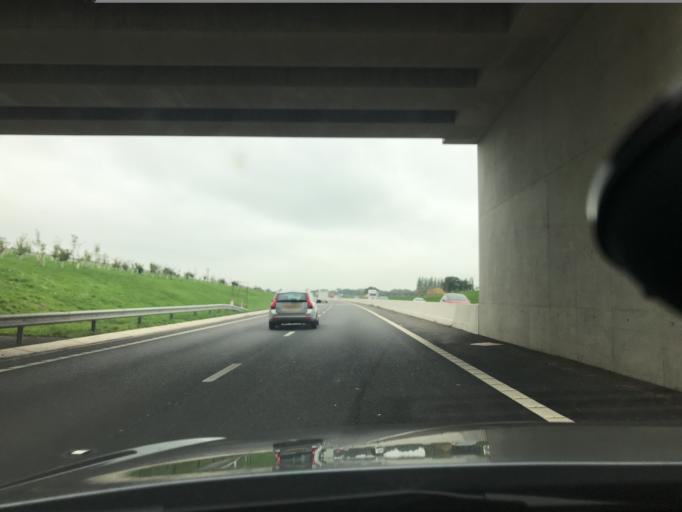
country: GB
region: England
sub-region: Cheshire East
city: Mere
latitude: 53.3204
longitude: -2.4205
